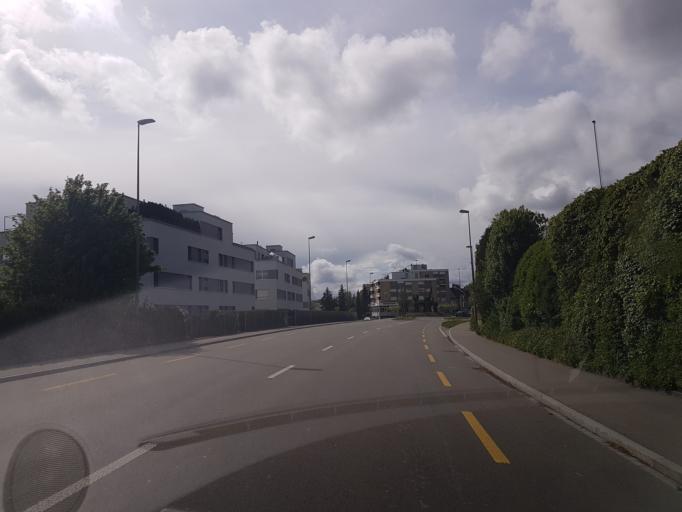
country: CH
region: Zurich
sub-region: Bezirk Dietikon
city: Unterengstringen
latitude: 47.4124
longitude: 8.4521
